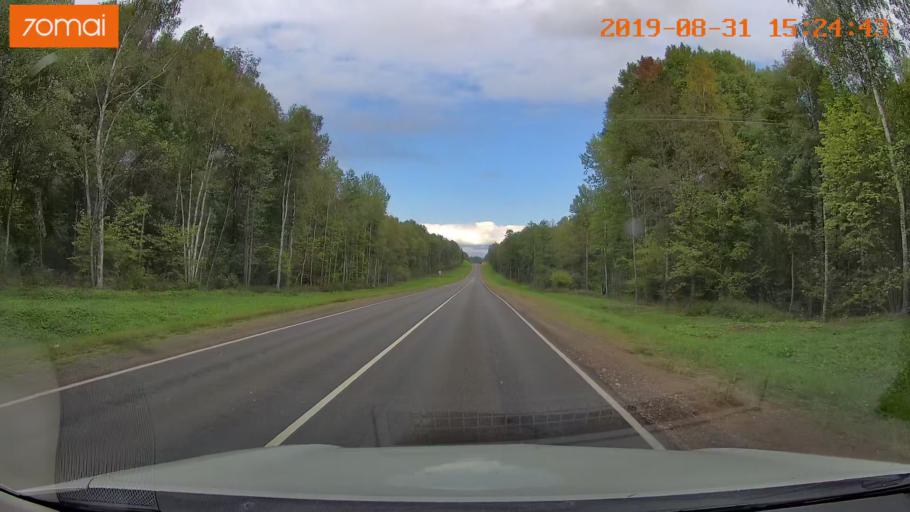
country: RU
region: Kaluga
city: Baryatino
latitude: 54.5316
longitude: 34.5089
